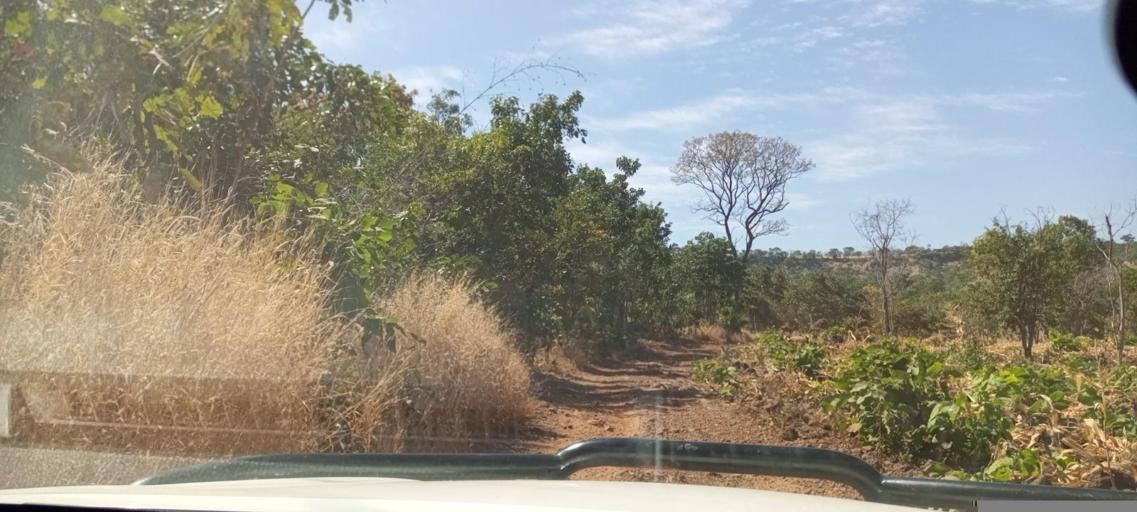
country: ML
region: Koulikoro
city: Kangaba
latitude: 12.3266
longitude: -8.6748
